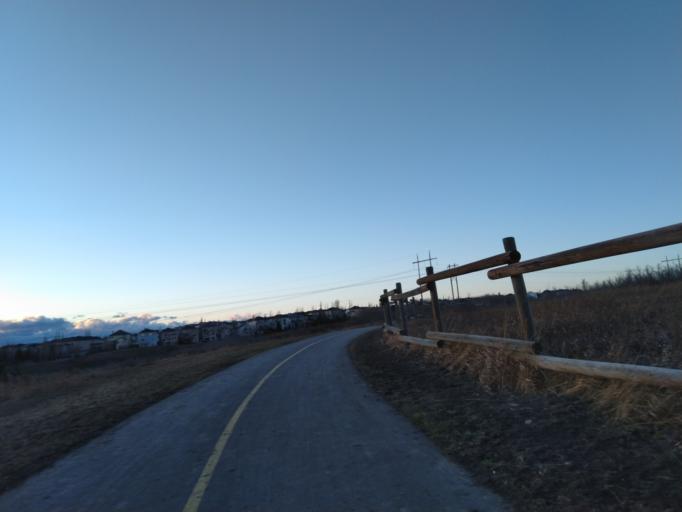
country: CA
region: Alberta
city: Calgary
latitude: 51.1154
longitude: -114.2327
